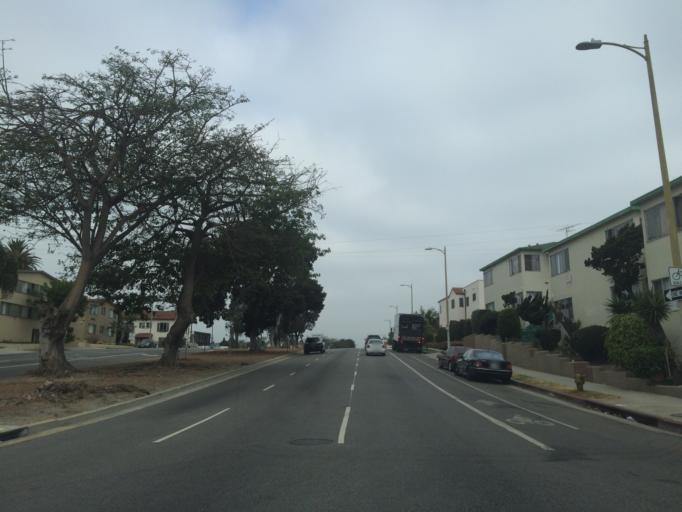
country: US
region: California
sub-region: Los Angeles County
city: West Hollywood
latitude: 34.0494
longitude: -118.3417
